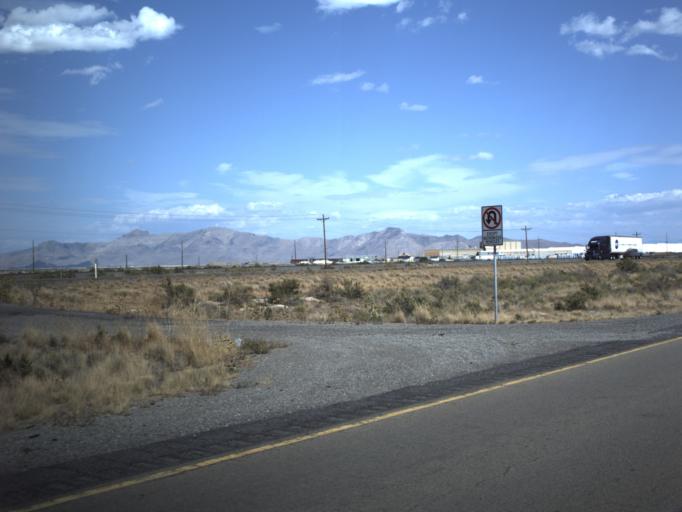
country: US
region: Utah
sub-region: Tooele County
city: Grantsville
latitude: 40.7473
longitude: -112.6700
